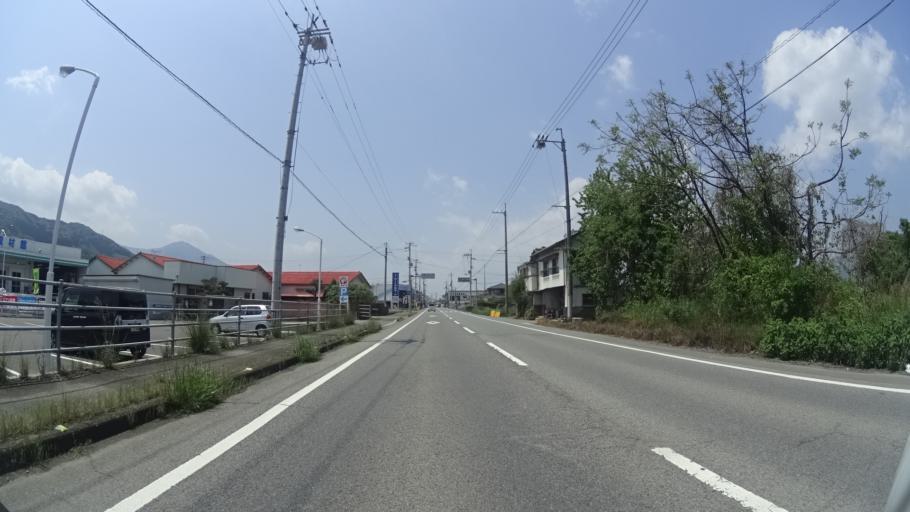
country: JP
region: Tokushima
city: Kamojimacho-jogejima
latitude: 34.0637
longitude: 134.2710
